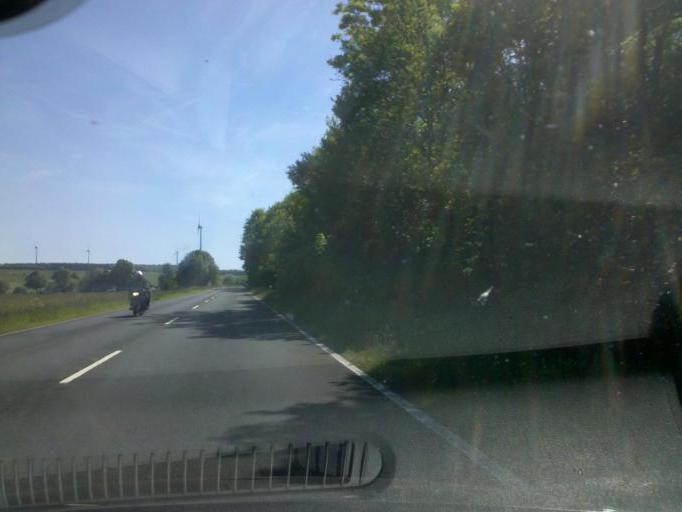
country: DE
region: Rheinland-Pfalz
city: Rehe
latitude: 50.6650
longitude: 8.1336
